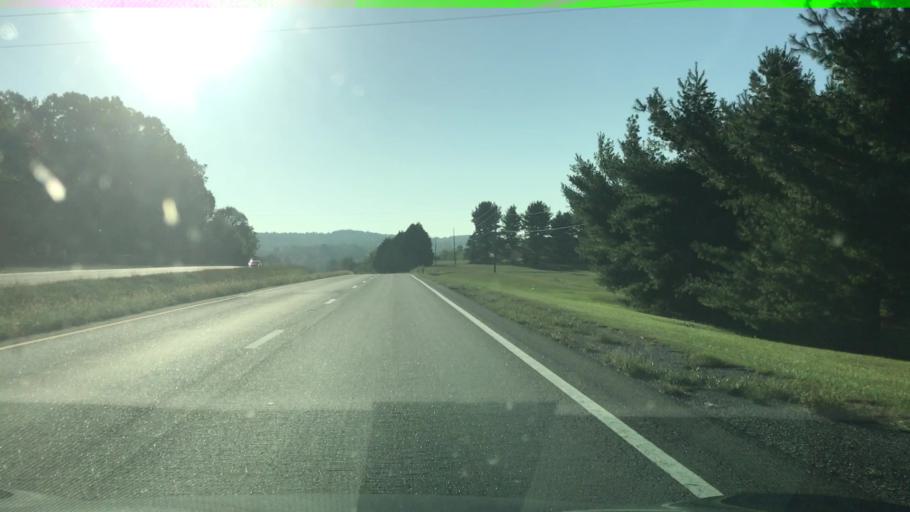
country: US
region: Virginia
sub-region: City of Bedford
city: Bedford
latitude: 37.3133
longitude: -79.4058
